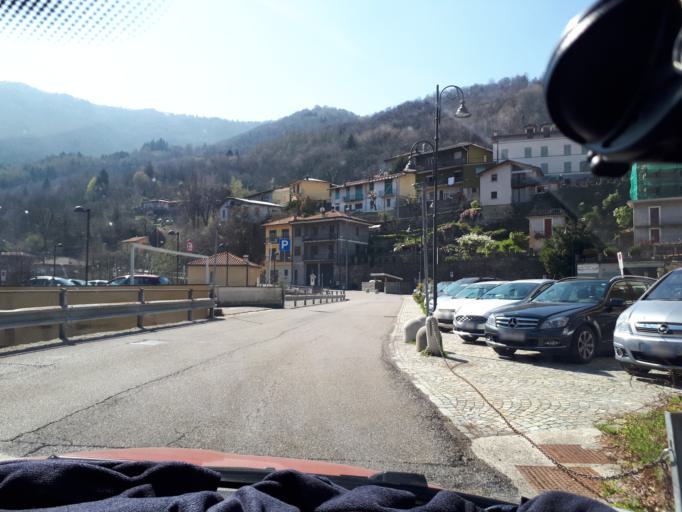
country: IT
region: Lombardy
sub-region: Provincia di Como
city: Faggeto Lario
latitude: 45.8584
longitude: 9.1540
